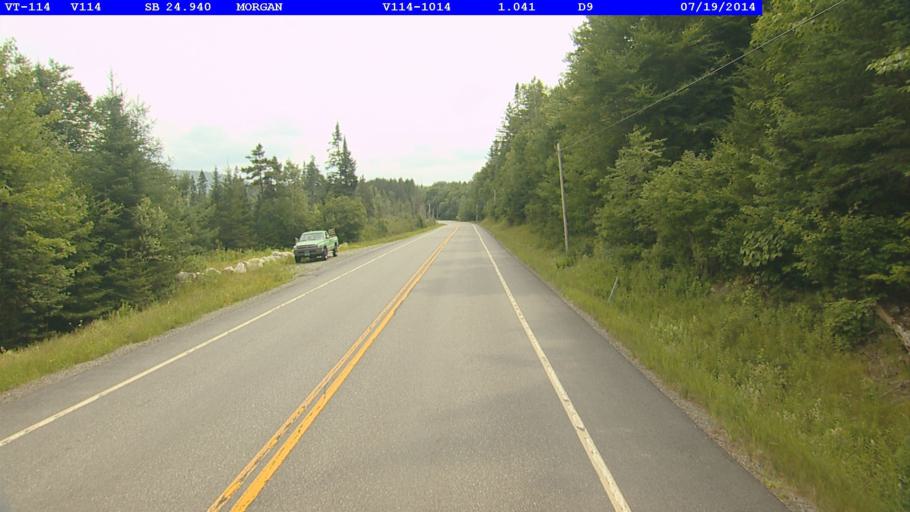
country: CA
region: Quebec
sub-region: Estrie
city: Coaticook
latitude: 44.8616
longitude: -71.9090
